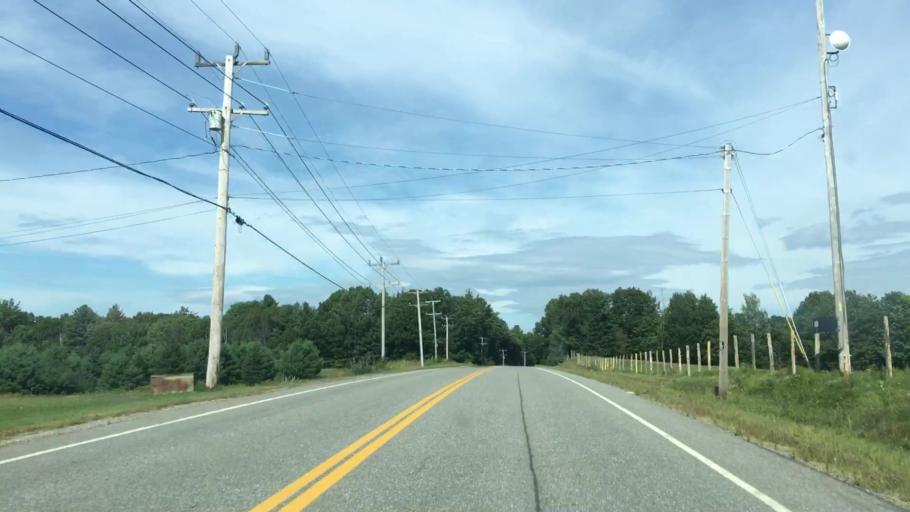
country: US
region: Maine
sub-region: Penobscot County
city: Lincoln
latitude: 45.3989
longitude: -68.5098
